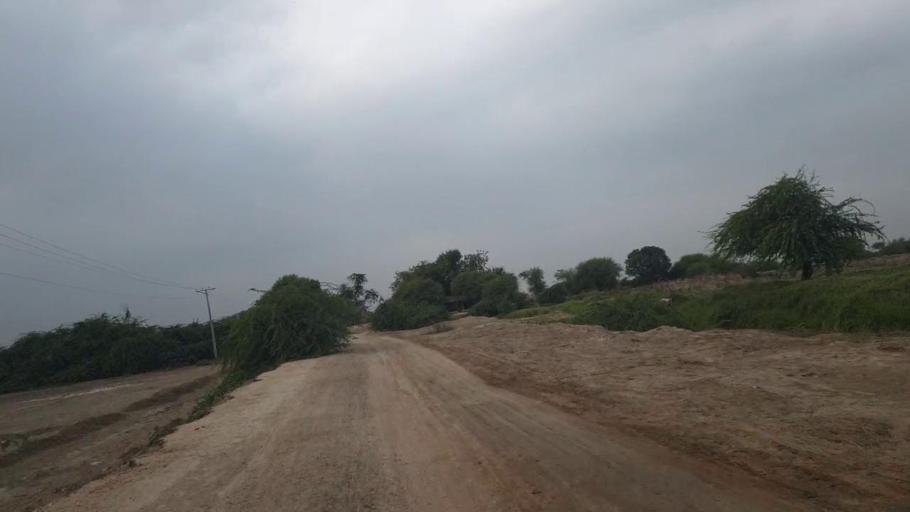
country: PK
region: Sindh
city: Badin
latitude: 24.6161
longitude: 68.6816
